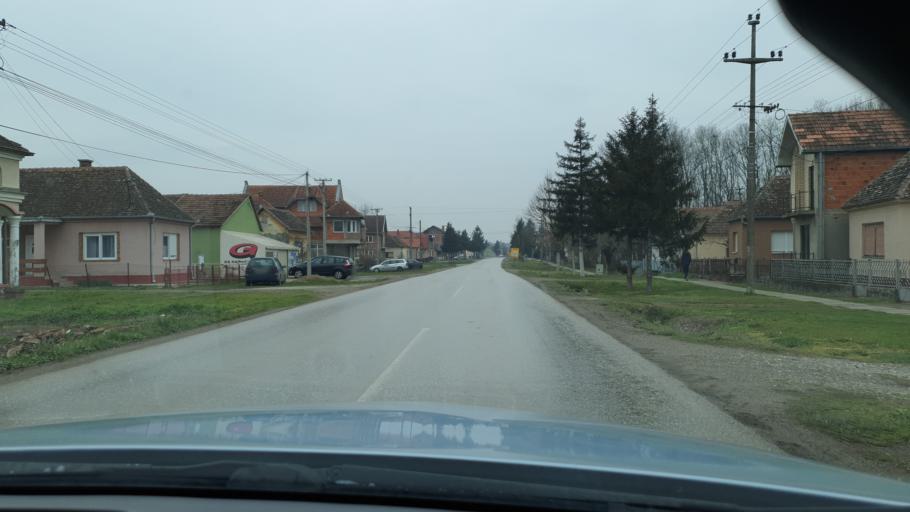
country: RS
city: Stitar
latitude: 44.7878
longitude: 19.5947
